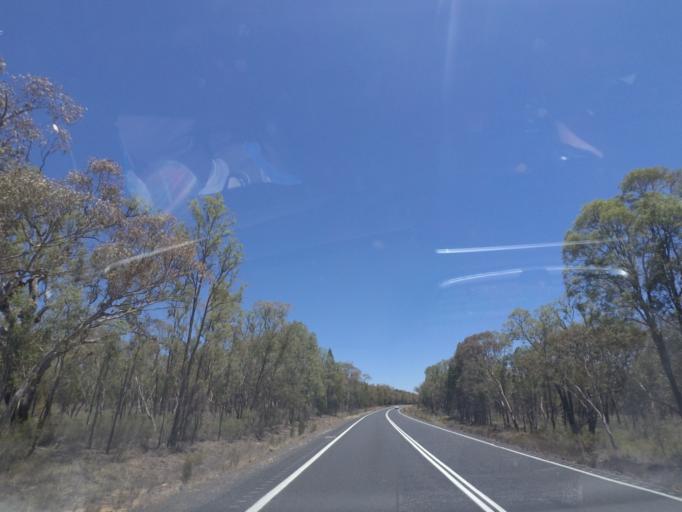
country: AU
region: New South Wales
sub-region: Warrumbungle Shire
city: Coonabarabran
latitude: -31.1958
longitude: 149.3507
